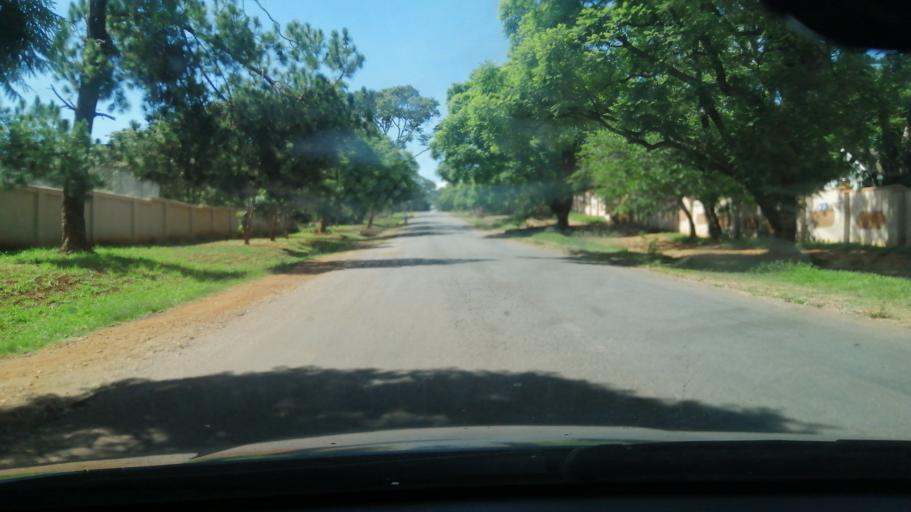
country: ZW
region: Harare
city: Harare
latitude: -17.7987
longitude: 31.1287
